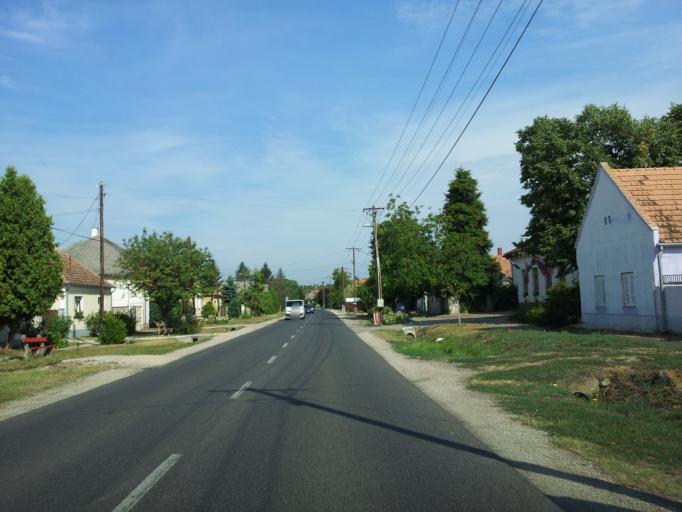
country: HU
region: Veszprem
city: Tapolca
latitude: 46.8693
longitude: 17.4795
